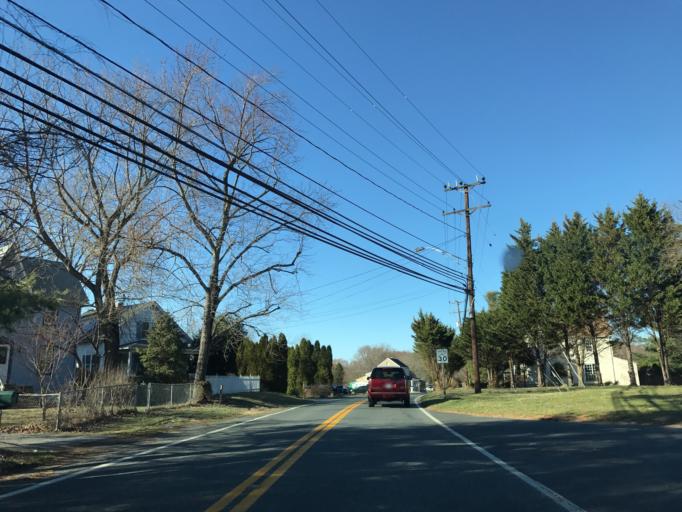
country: US
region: Maryland
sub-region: Harford County
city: Perryman
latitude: 39.4687
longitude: -76.2043
